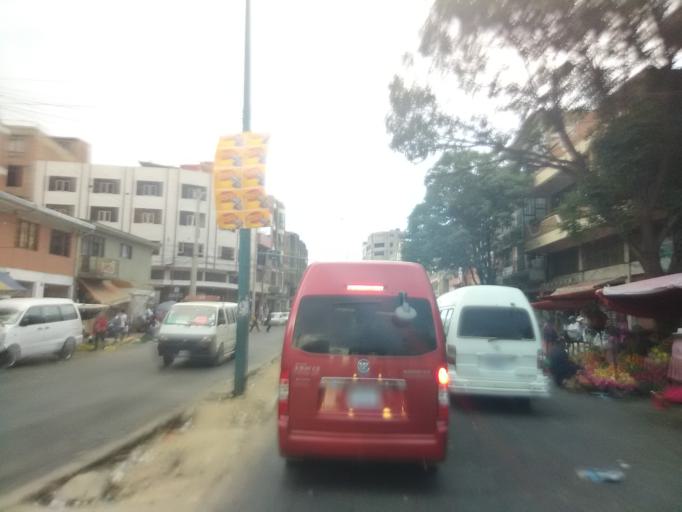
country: BO
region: Cochabamba
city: Cochabamba
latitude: -17.3985
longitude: -66.1516
